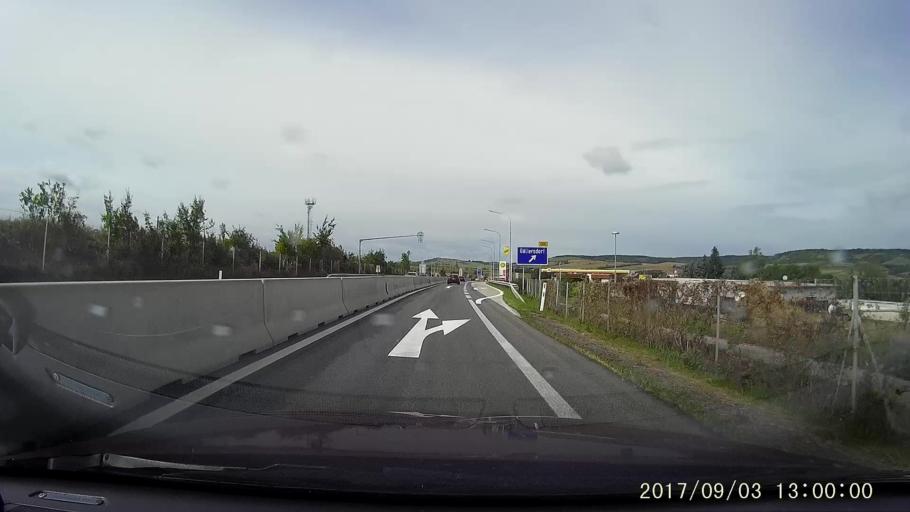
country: AT
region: Lower Austria
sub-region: Politischer Bezirk Hollabrunn
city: Gollersdorf
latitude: 48.4908
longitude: 16.1105
